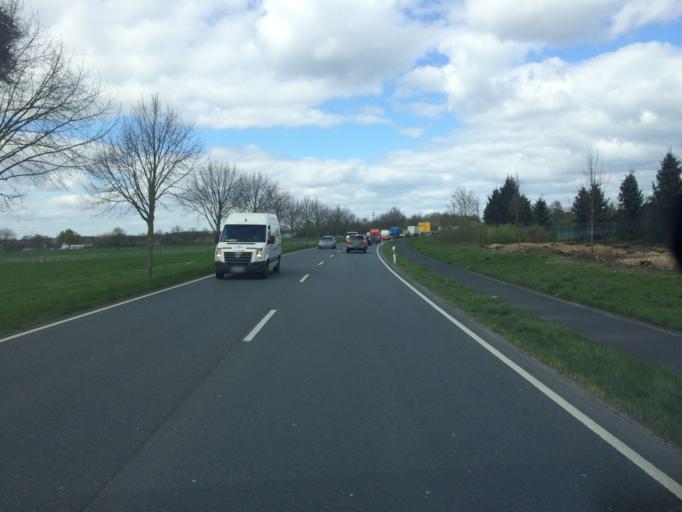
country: DE
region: North Rhine-Westphalia
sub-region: Regierungsbezirk Munster
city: Coesfeld
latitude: 51.9265
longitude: 7.1563
